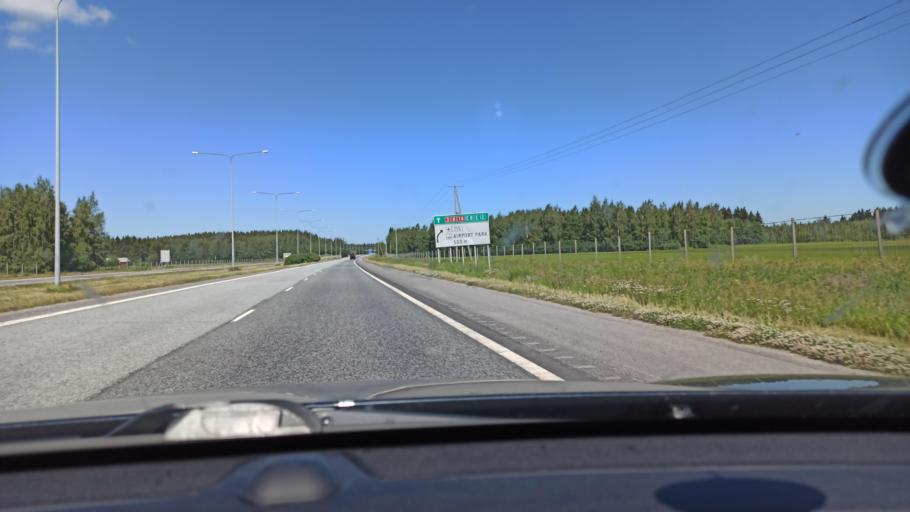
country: FI
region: Ostrobothnia
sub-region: Vaasa
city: Ristinummi
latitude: 63.0451
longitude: 21.7250
